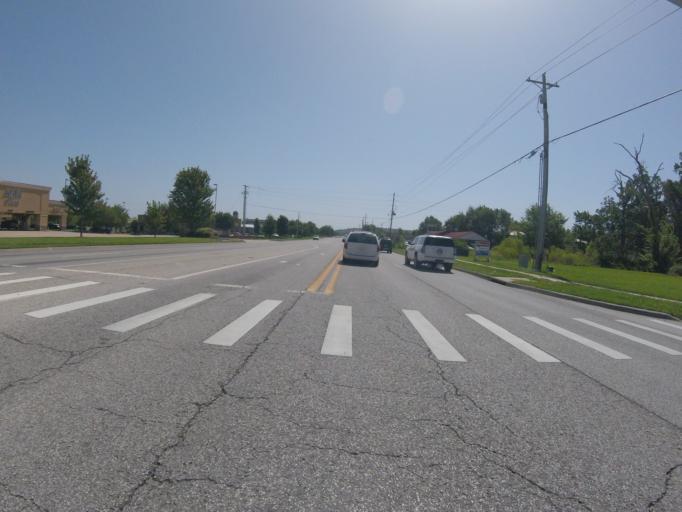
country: US
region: Arkansas
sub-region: Washington County
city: Fayetteville
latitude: 36.0784
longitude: -94.2081
